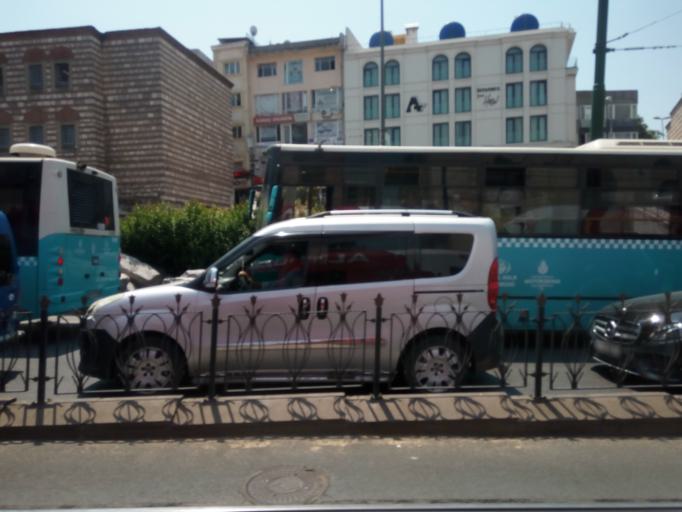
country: TR
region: Istanbul
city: Istanbul
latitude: 41.0095
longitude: 28.9625
